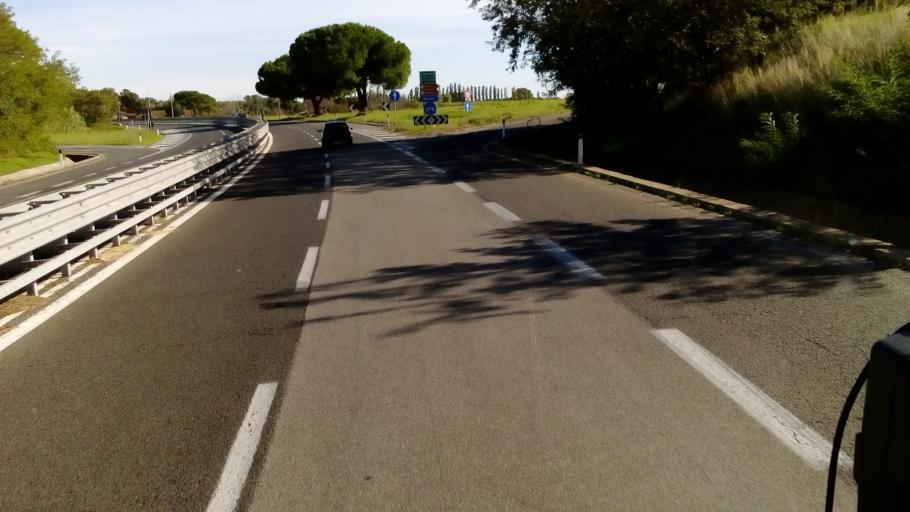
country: IT
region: Latium
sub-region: Provincia di Viterbo
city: Montalto di Castro
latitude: 42.3098
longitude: 11.6547
